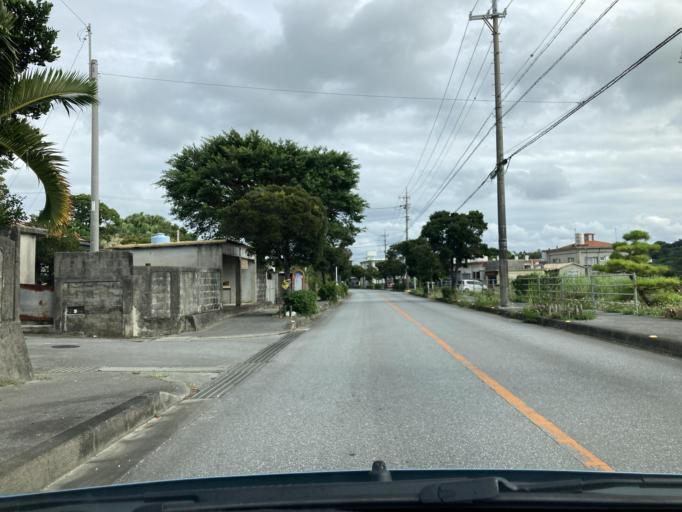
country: JP
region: Okinawa
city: Itoman
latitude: 26.1209
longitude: 127.6811
